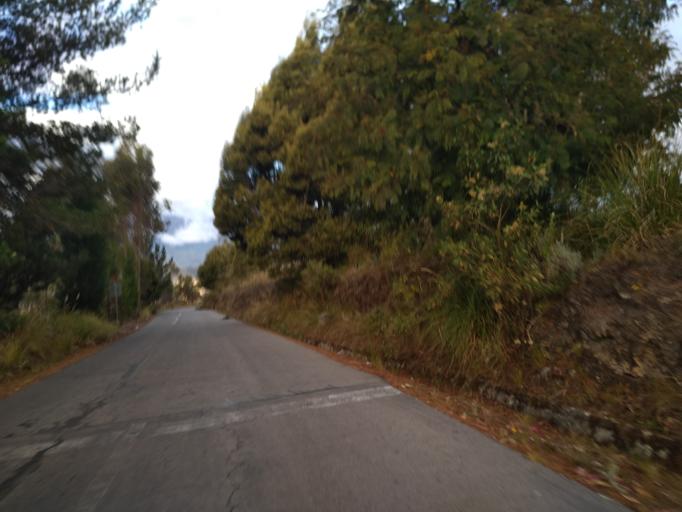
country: EC
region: Chimborazo
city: Riobamba
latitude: -1.7030
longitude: -78.7080
